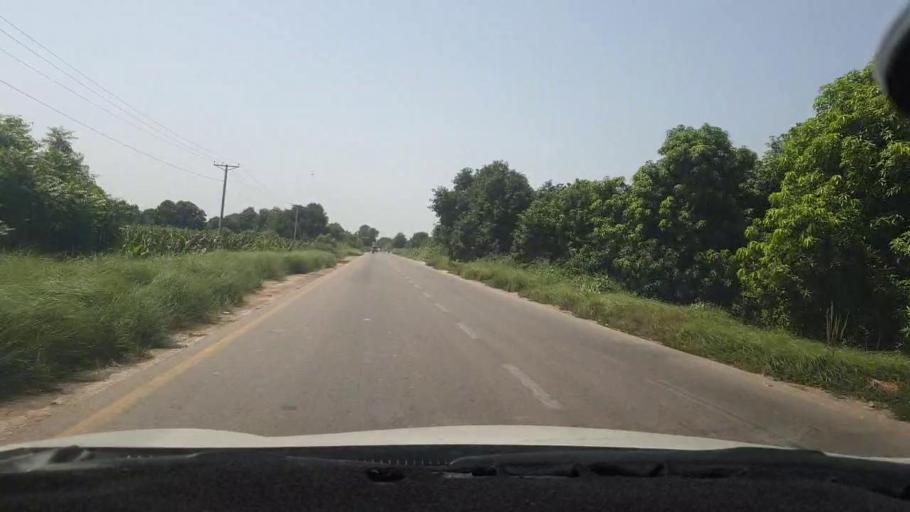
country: PK
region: Sindh
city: Bhit Shah
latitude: 25.8588
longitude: 68.5067
